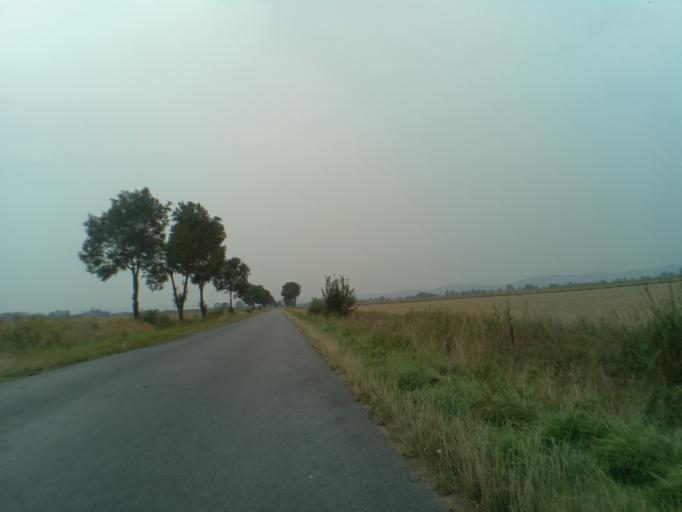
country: PL
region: Lower Silesian Voivodeship
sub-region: Powiat swidnicki
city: Strzegom
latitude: 50.9249
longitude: 16.3233
